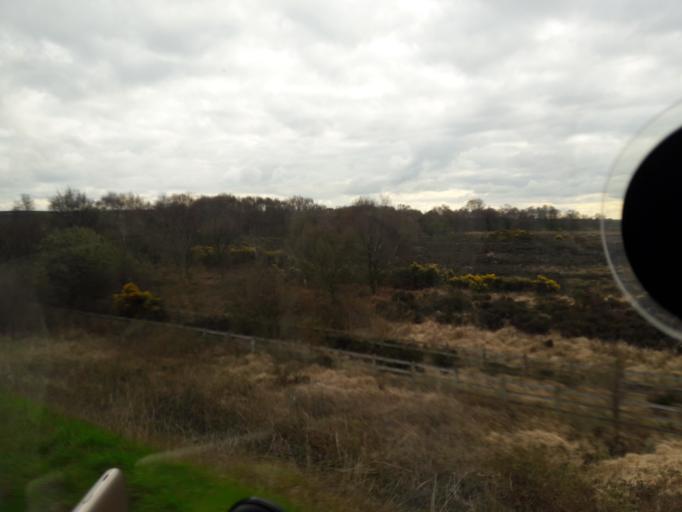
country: IE
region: Leinster
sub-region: An Longfort
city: Granard
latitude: 53.6537
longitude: -7.4360
